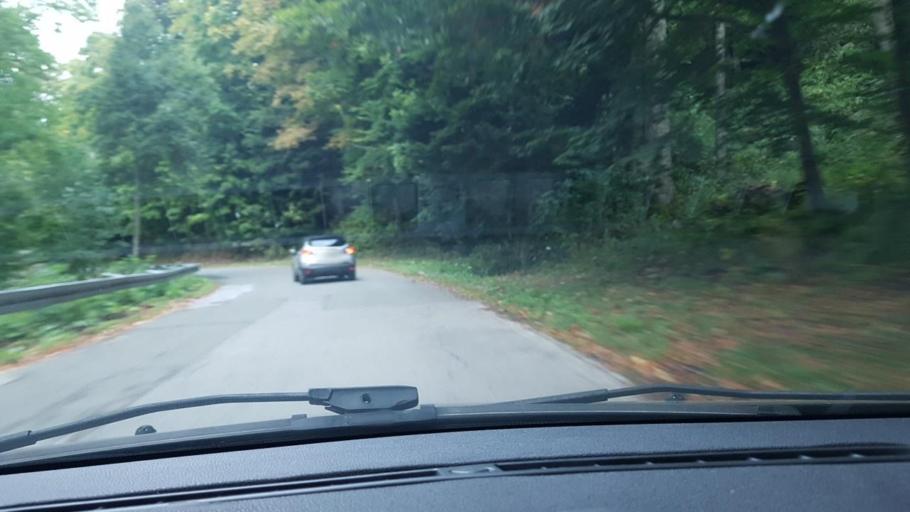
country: HR
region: Grad Zagreb
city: Kasina
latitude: 45.8966
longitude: 15.9434
